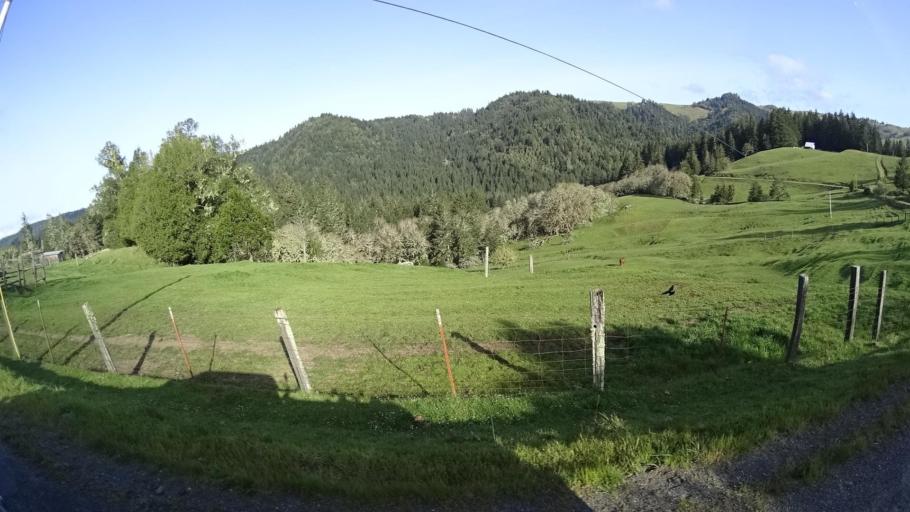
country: US
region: California
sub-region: Humboldt County
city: Bayside
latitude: 40.6878
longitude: -123.9379
